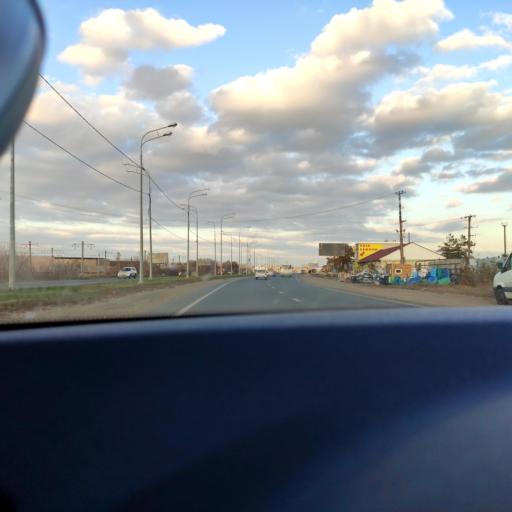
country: RU
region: Samara
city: Smyshlyayevka
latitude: 53.2587
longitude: 50.3759
